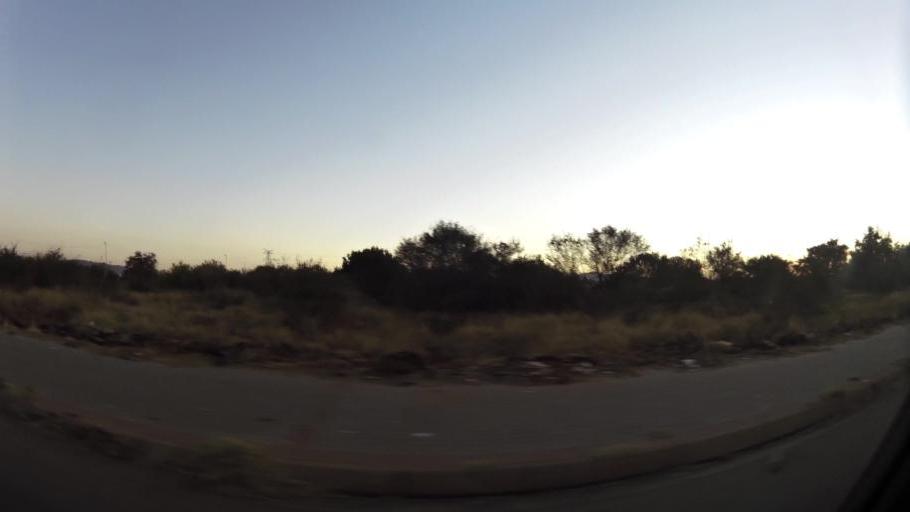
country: ZA
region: North-West
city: Ga-Rankuwa
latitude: -25.6002
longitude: 27.9915
